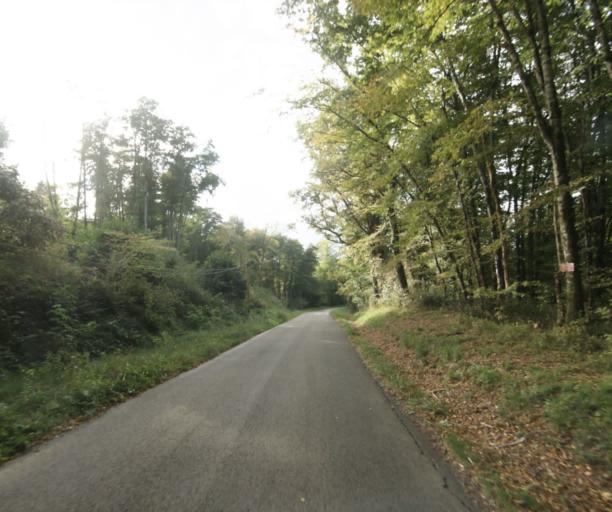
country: FR
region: Midi-Pyrenees
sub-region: Departement du Gers
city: Eauze
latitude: 43.8767
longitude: 0.0873
